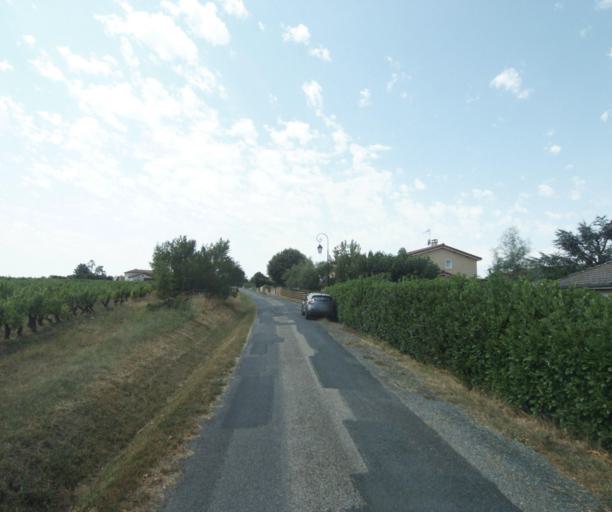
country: FR
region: Rhone-Alpes
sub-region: Departement du Rhone
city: Saint-Germain-Nuelles
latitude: 45.8480
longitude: 4.6237
